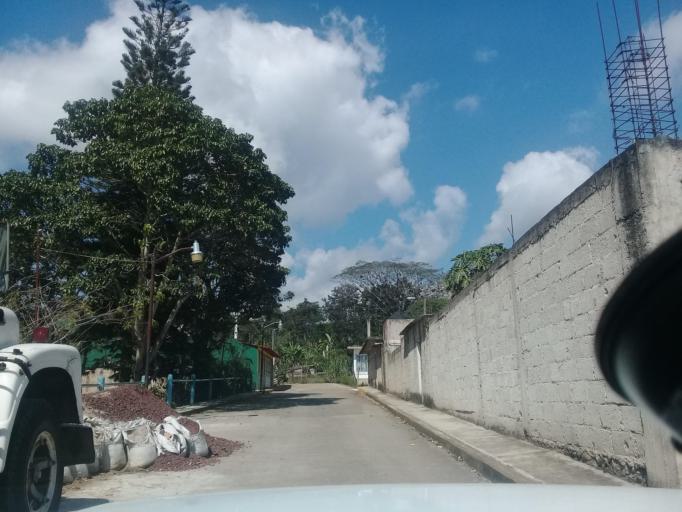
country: MX
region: Veracruz
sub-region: Coatepec
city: Bella Esperanza
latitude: 19.4335
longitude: -96.8682
